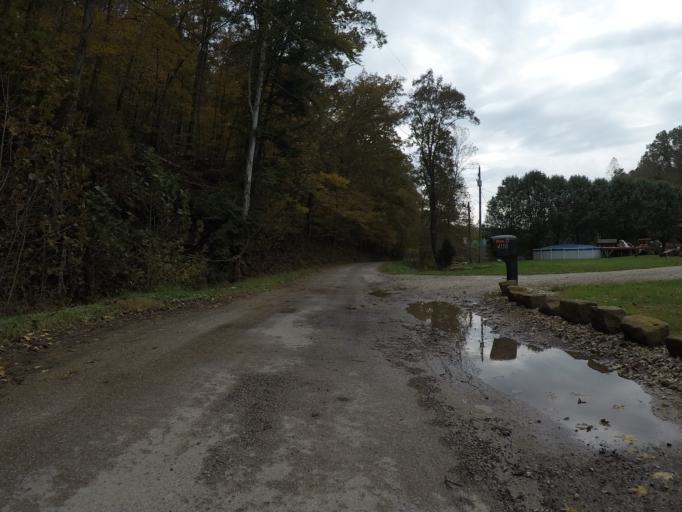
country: US
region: West Virginia
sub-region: Wayne County
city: Lavalette
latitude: 38.3541
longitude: -82.4187
